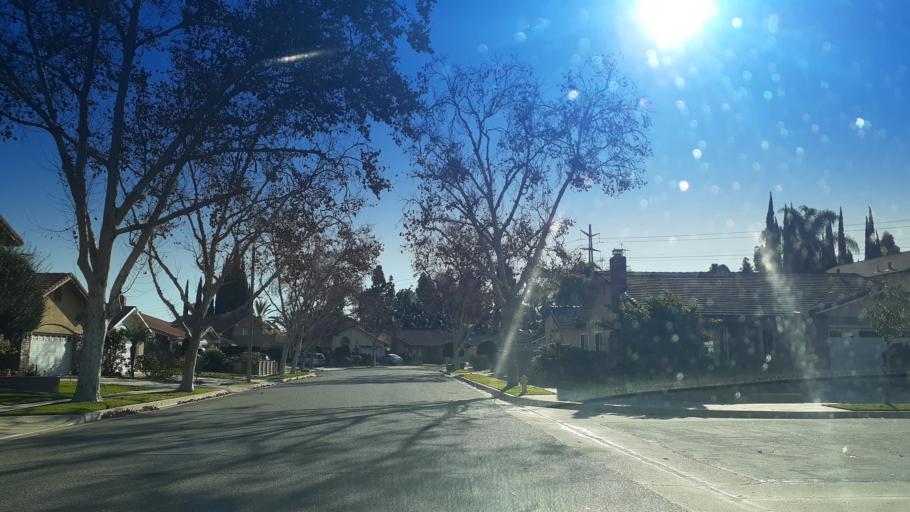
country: US
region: California
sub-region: Los Angeles County
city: Cerritos
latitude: 33.8517
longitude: -118.0691
